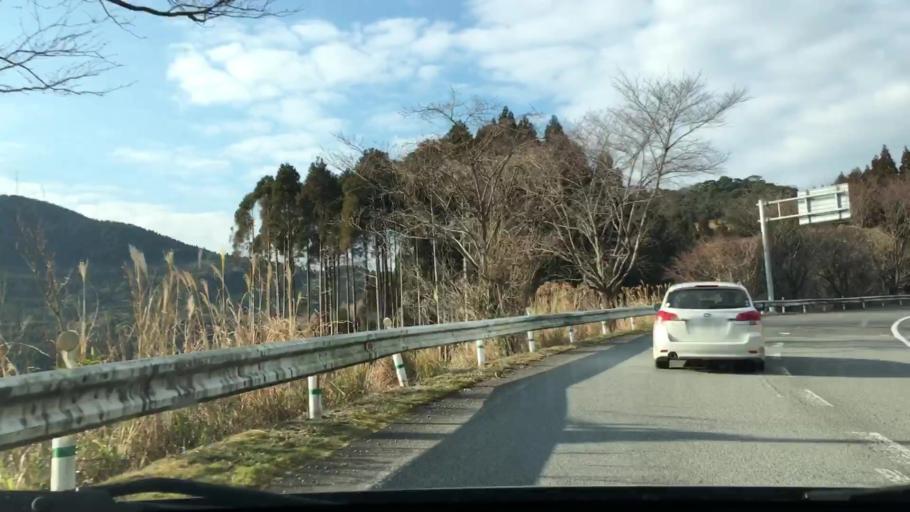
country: JP
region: Miyazaki
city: Miyazaki-shi
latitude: 31.7771
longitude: 131.3305
